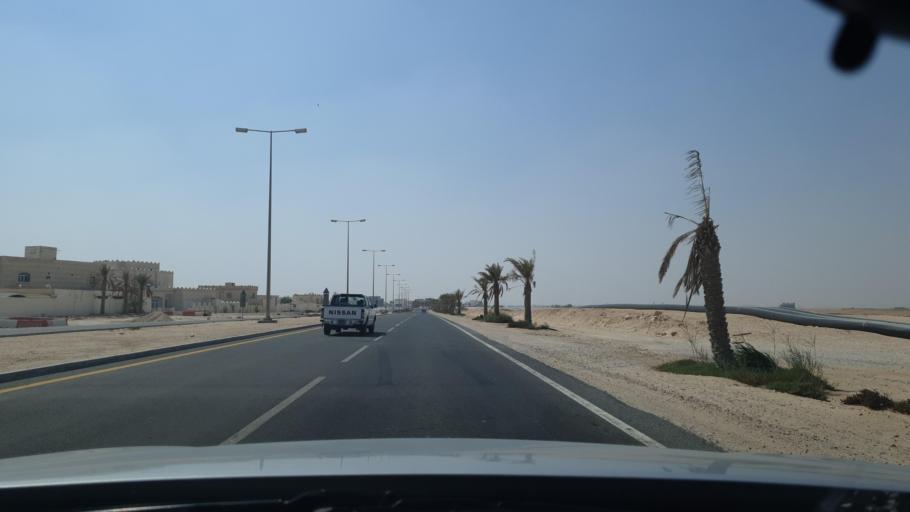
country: QA
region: Al Khawr
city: Al Khawr
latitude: 25.6833
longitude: 51.4802
